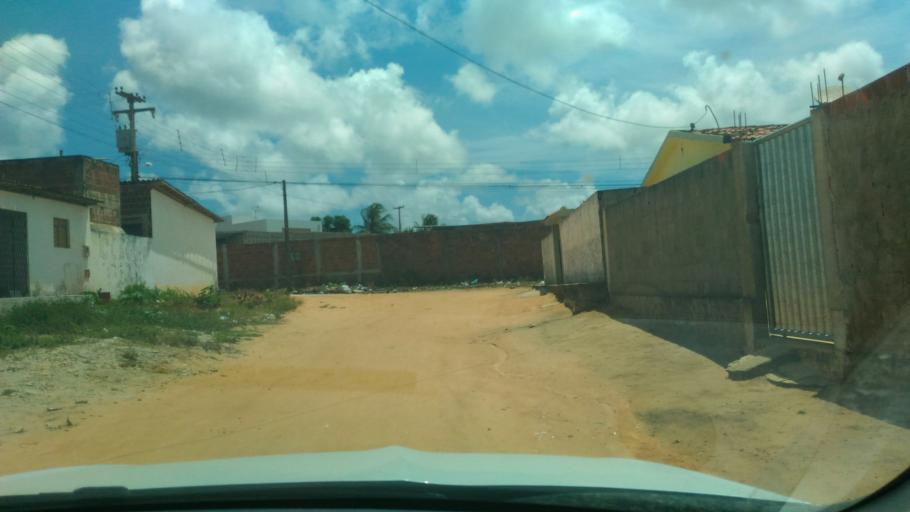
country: BR
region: Paraiba
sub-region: Conde
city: Conde
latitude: -7.2629
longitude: -34.9112
